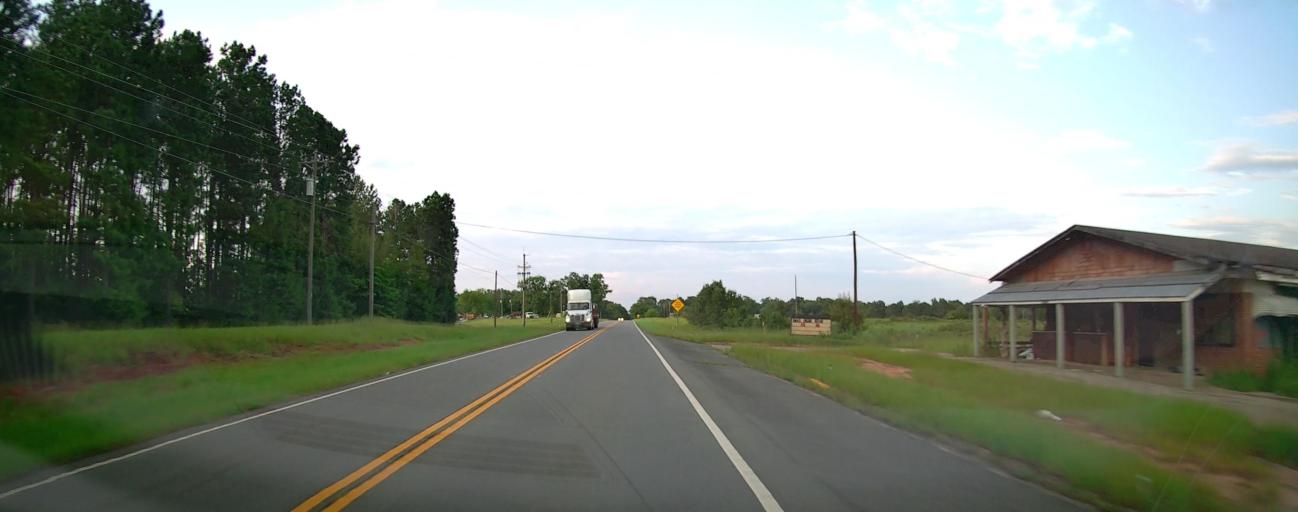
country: US
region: Georgia
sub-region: Crawford County
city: Roberta
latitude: 32.6749
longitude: -84.0901
